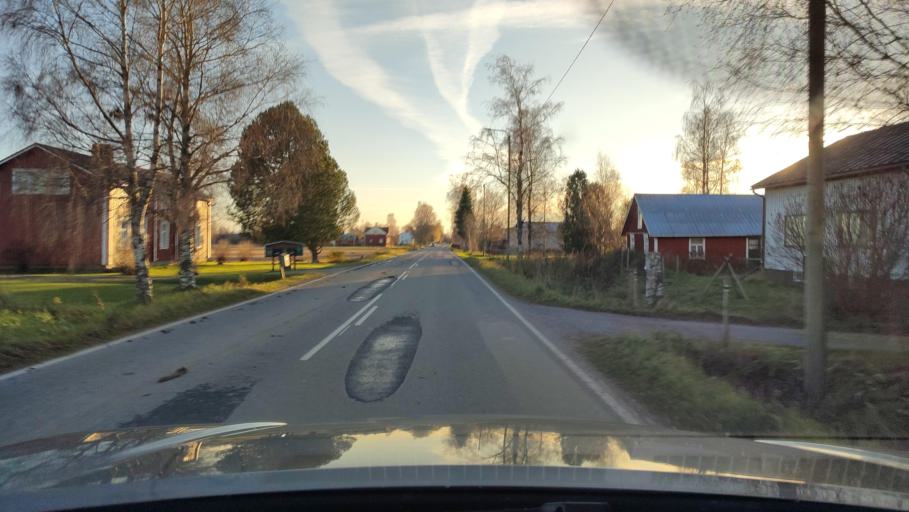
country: FI
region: Ostrobothnia
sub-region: Sydosterbotten
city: Naerpes
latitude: 62.6207
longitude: 21.4824
